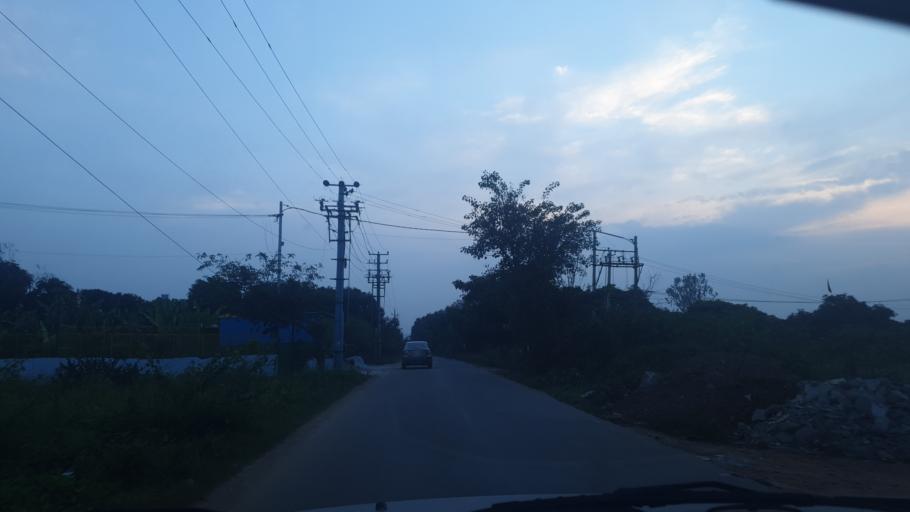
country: IN
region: Karnataka
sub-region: Bangalore Urban
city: Yelahanka
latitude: 13.0588
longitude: 77.6848
